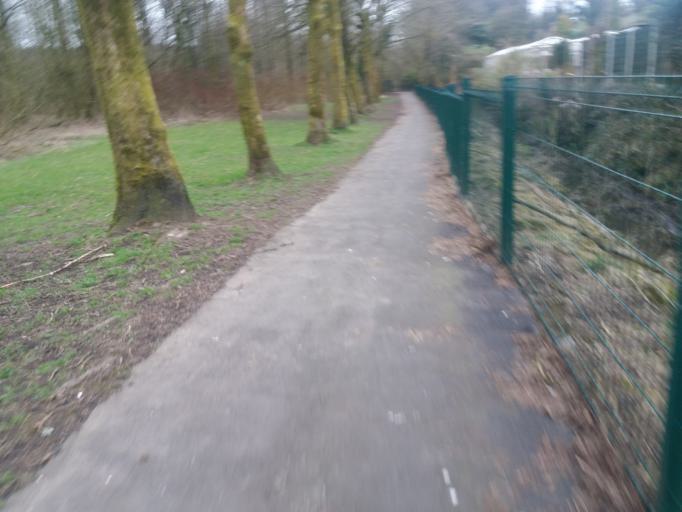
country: GB
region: England
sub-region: Lancashire
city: Chorley
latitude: 53.6670
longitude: -2.6278
